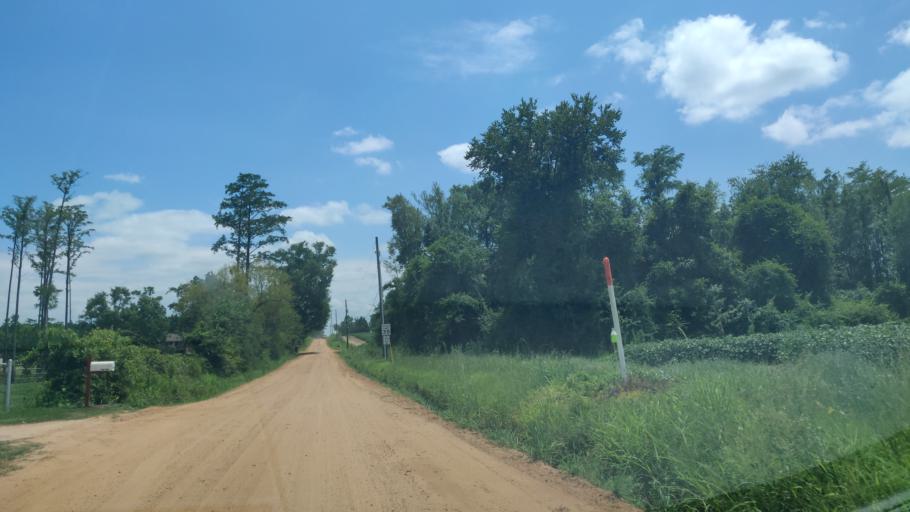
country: US
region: Georgia
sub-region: Tift County
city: Tifton
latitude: 31.4711
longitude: -83.6373
